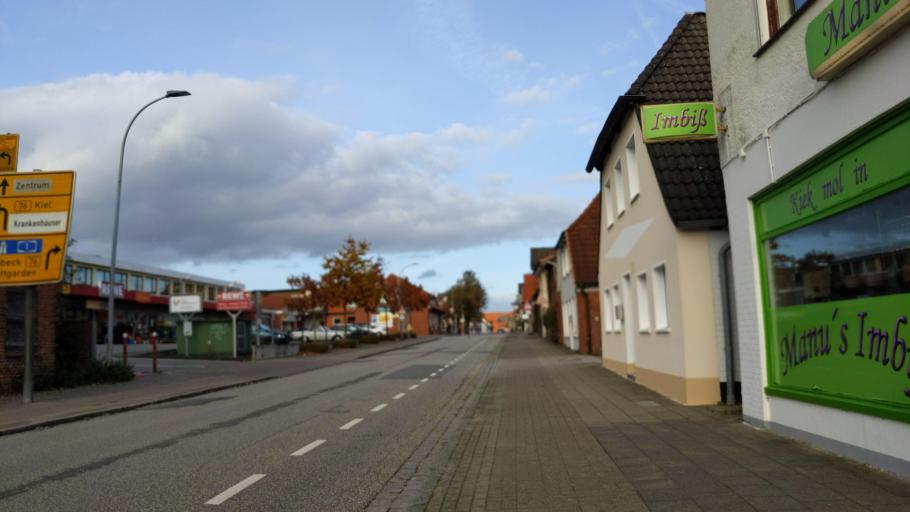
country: DE
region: Schleswig-Holstein
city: Eutin
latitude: 54.1298
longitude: 10.6156
